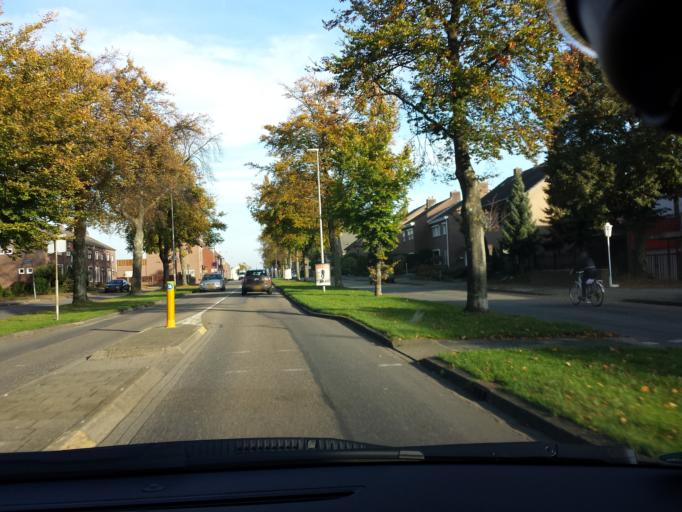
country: NL
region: Limburg
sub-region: Gemeente Kerkrade
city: Kerkrade
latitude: 50.8653
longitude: 6.0370
